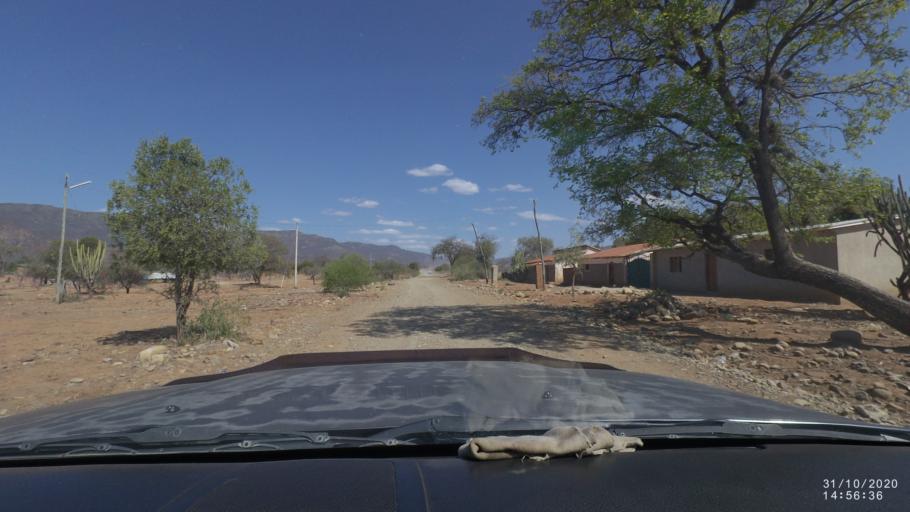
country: BO
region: Cochabamba
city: Aiquile
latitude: -18.2393
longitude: -64.8493
